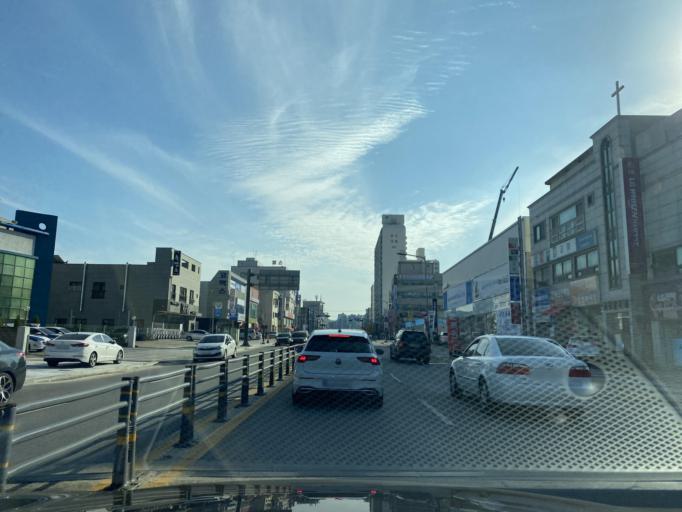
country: KR
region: Chungcheongnam-do
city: Cheonan
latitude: 36.8049
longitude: 127.1588
